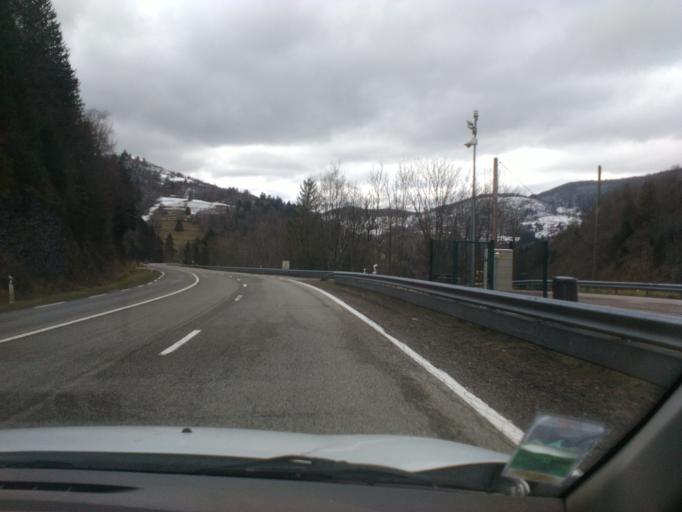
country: FR
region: Lorraine
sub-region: Departement des Vosges
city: Bussang
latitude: 47.8889
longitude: 6.8898
